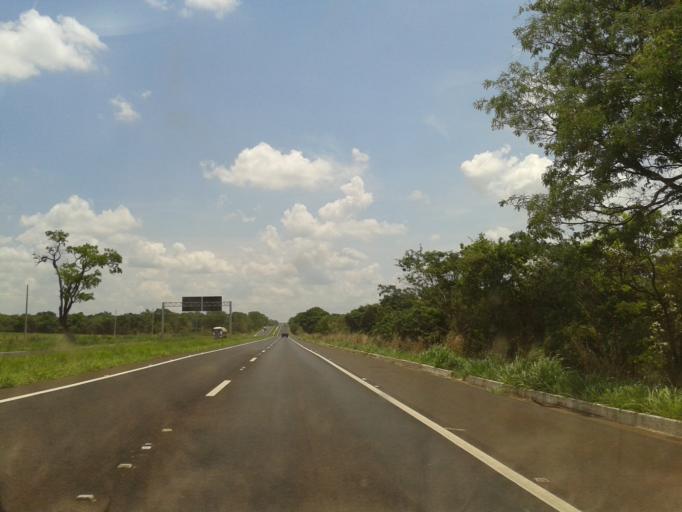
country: BR
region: Minas Gerais
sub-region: Monte Alegre De Minas
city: Monte Alegre de Minas
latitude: -18.8684
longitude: -48.7584
